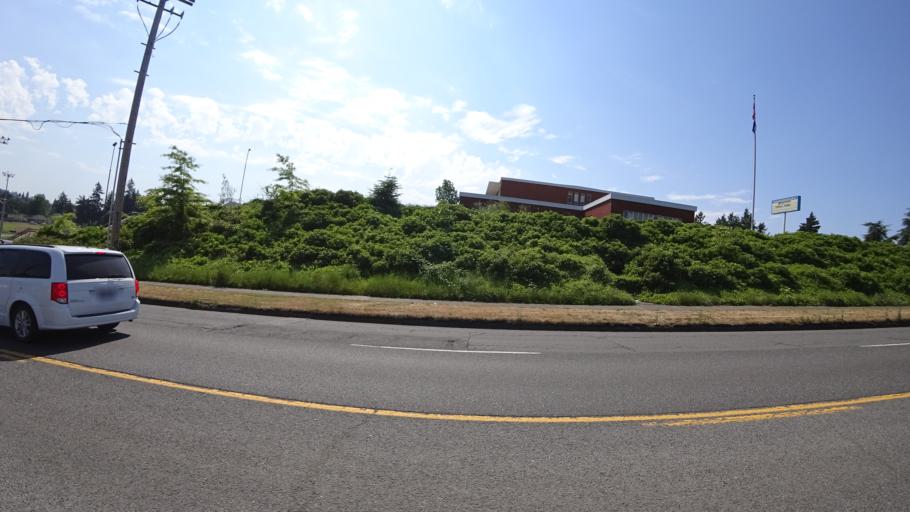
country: US
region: Oregon
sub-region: Multnomah County
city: Lents
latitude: 45.5417
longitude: -122.5788
